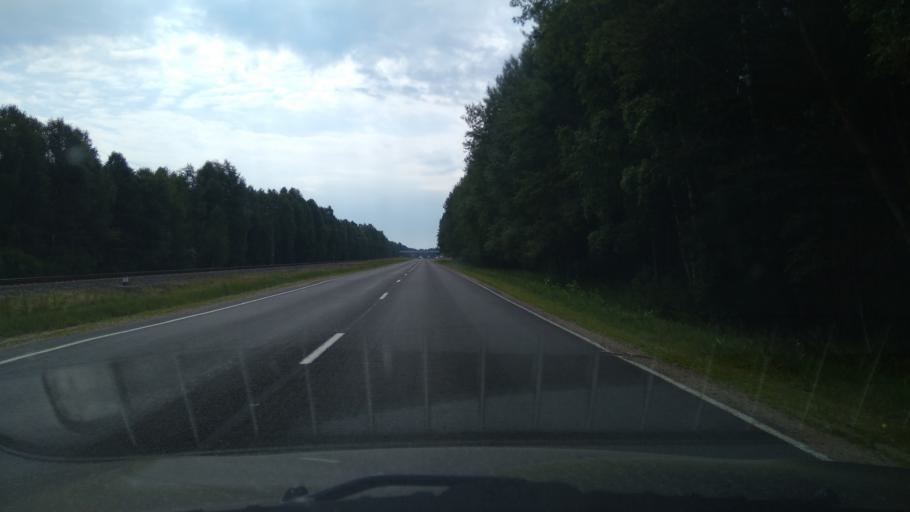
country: BY
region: Brest
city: Nyakhachava
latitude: 52.5819
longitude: 25.1031
